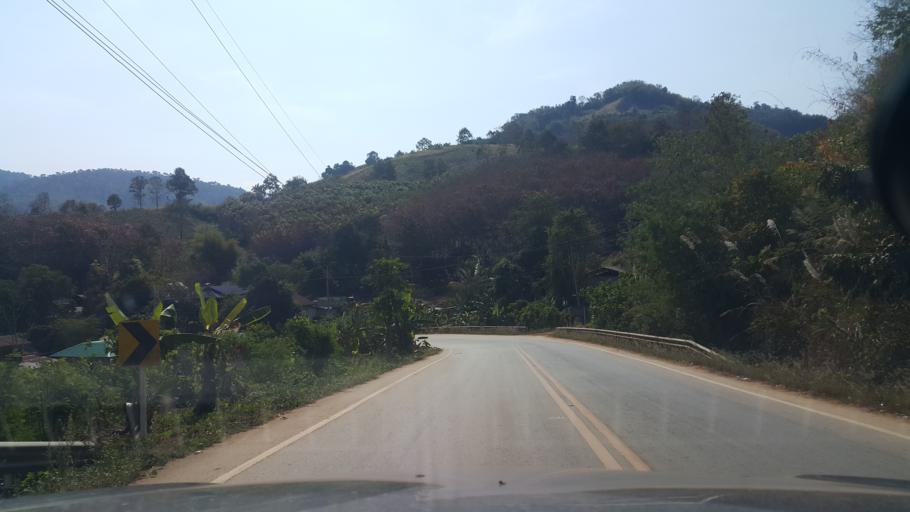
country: TH
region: Loei
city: Pak Chom
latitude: 18.1014
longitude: 102.0219
